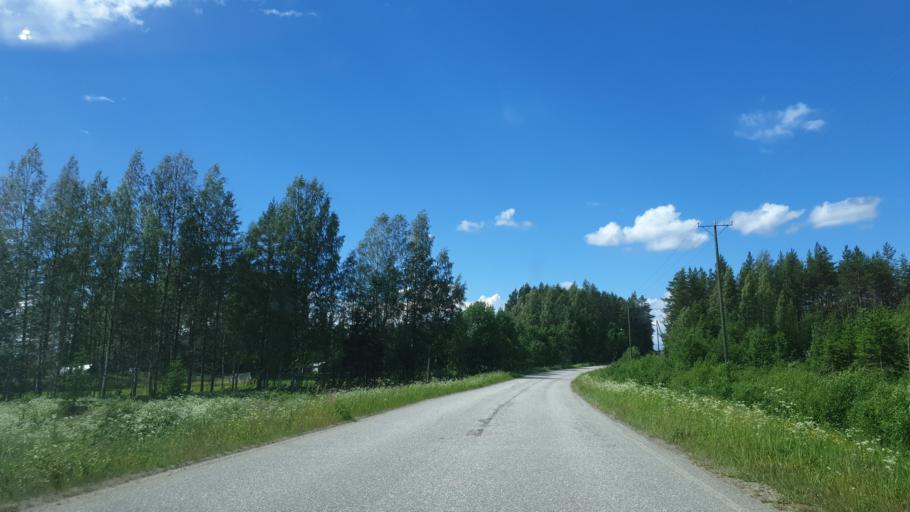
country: FI
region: Northern Savo
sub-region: Koillis-Savo
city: Kaavi
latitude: 62.9991
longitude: 28.6965
